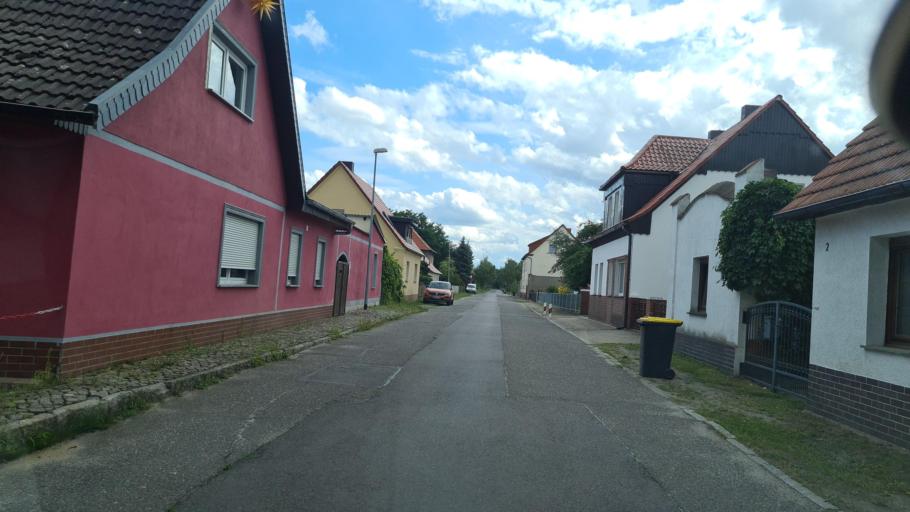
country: DE
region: Brandenburg
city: Drebkau
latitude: 51.6530
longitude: 14.2229
